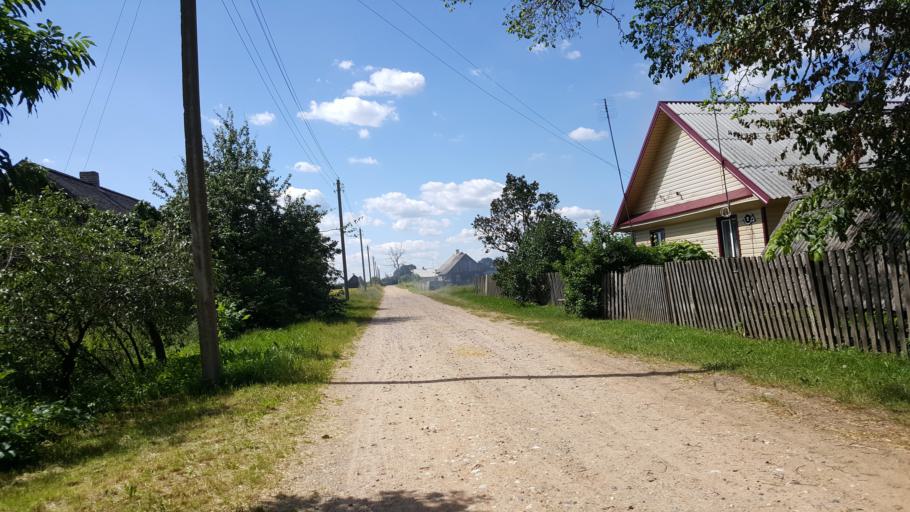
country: BY
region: Brest
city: Kamyanyuki
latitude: 52.5355
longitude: 23.6026
